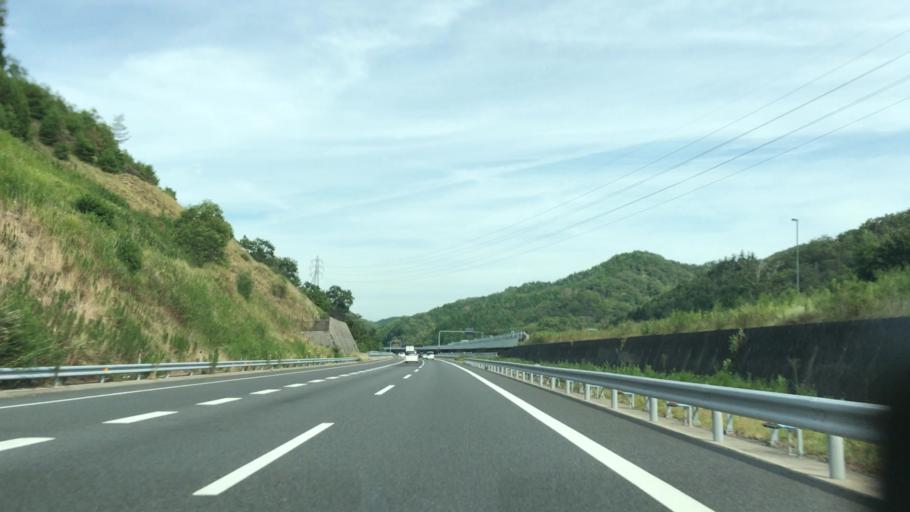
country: JP
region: Shiga Prefecture
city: Minakuchicho-matoba
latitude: 34.9245
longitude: 136.0894
